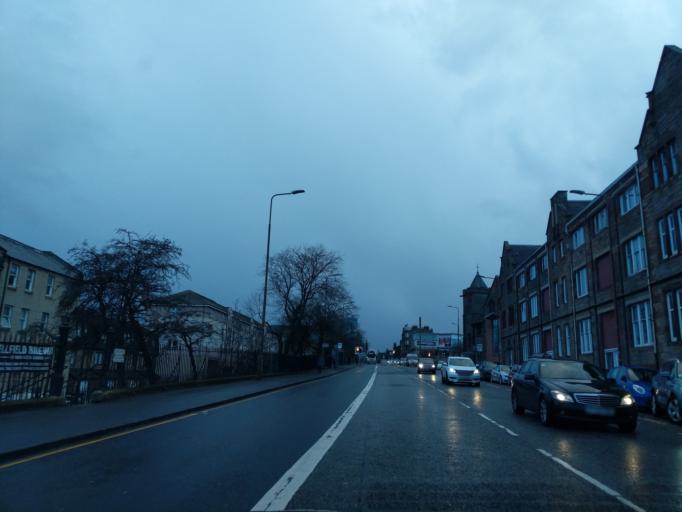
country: GB
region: Scotland
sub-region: West Lothian
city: Seafield
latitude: 55.9567
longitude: -3.1628
